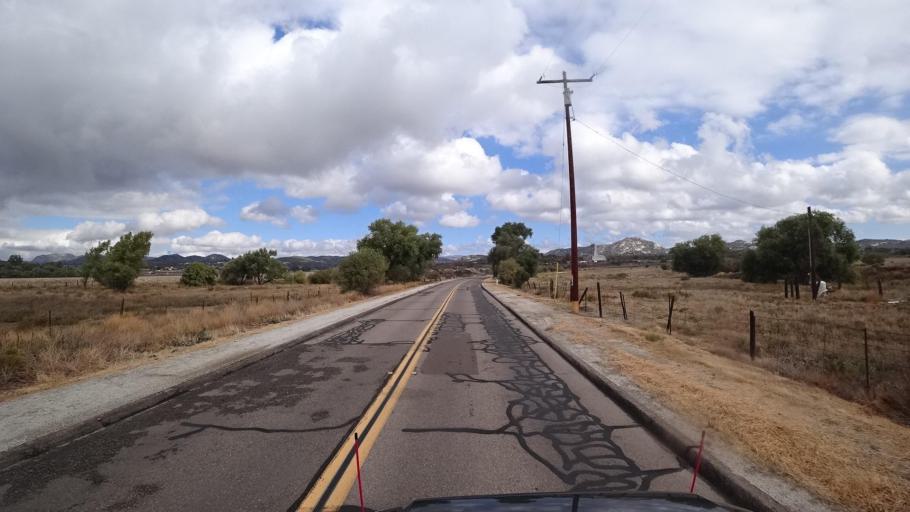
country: US
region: California
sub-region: San Diego County
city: Campo
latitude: 32.6249
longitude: -116.4629
